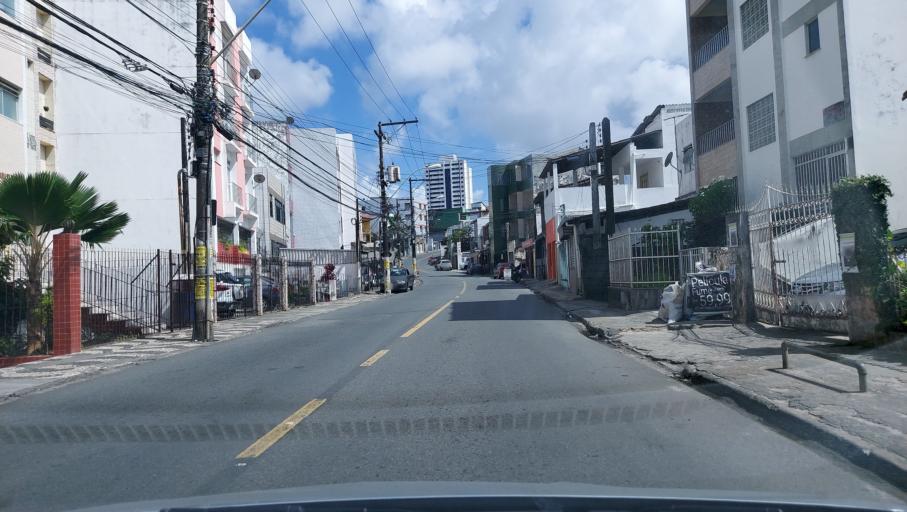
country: BR
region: Bahia
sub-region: Salvador
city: Salvador
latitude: -12.9906
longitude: -38.4782
